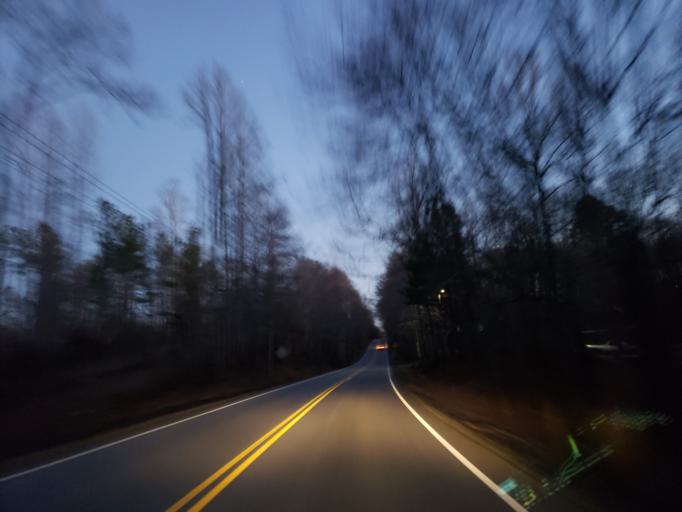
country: US
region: Georgia
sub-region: Bartow County
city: Emerson
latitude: 34.0774
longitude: -84.8331
